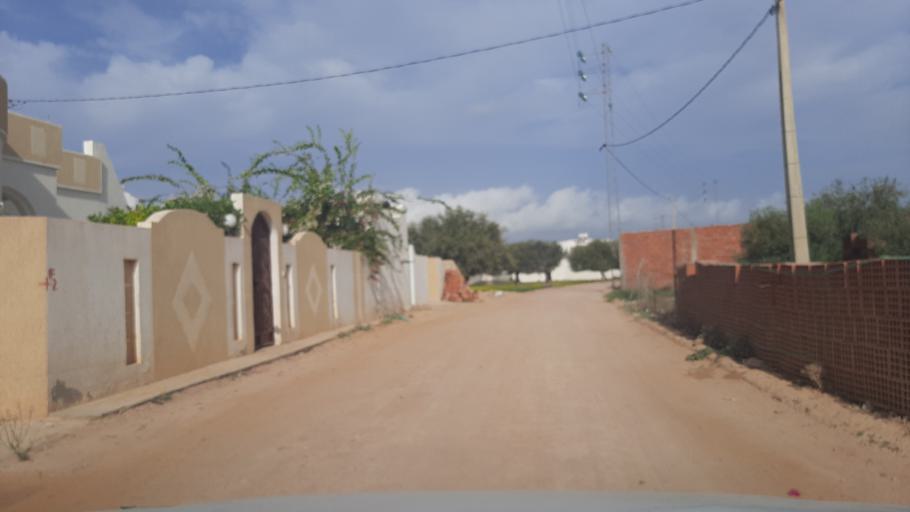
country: TN
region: Madanin
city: Midoun
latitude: 33.7994
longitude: 11.0279
